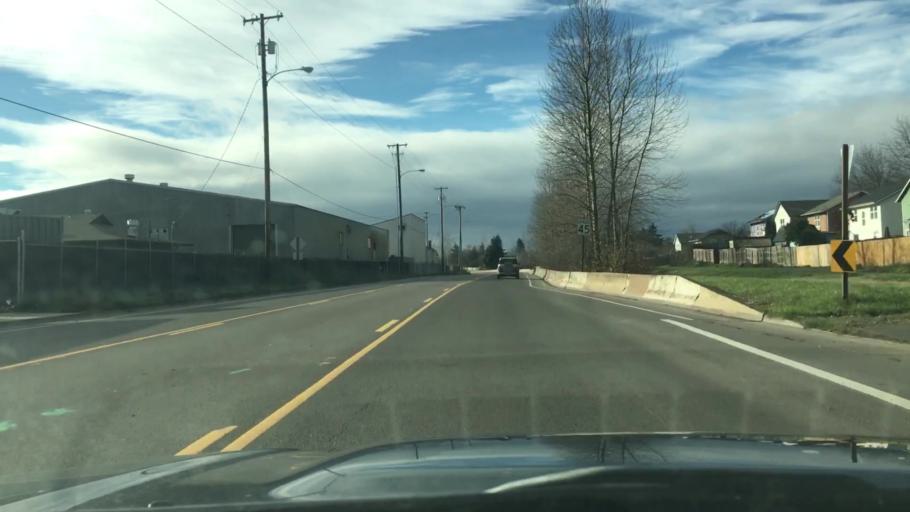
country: US
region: Oregon
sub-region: Lane County
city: Eugene
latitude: 44.0639
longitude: -123.1440
